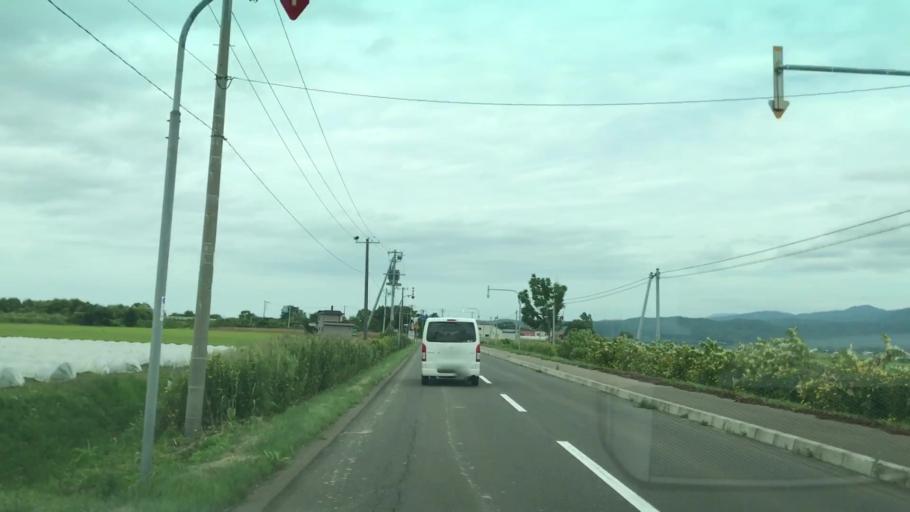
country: JP
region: Hokkaido
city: Iwanai
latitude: 43.0009
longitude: 140.5883
